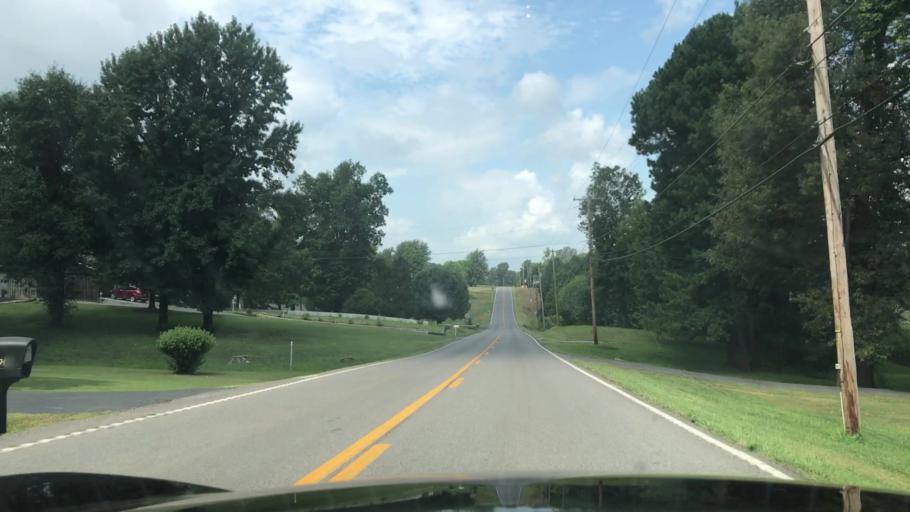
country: US
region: Kentucky
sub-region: Muhlenberg County
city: Greenville
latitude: 37.2054
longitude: -87.1489
